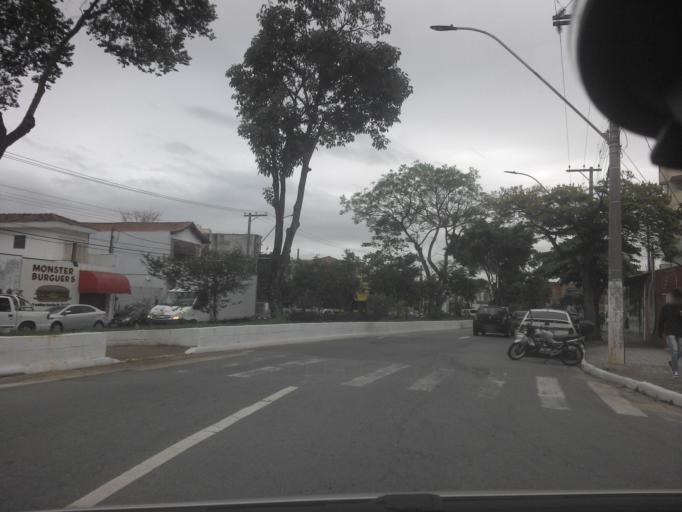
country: BR
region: Sao Paulo
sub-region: Taubate
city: Taubate
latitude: -23.0320
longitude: -45.5567
